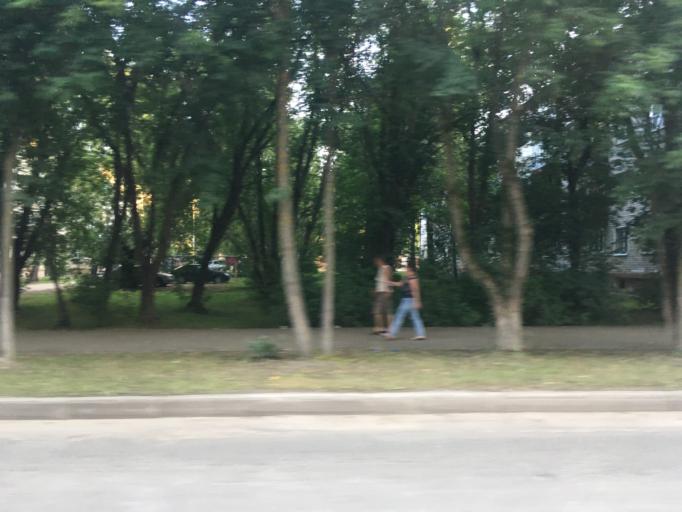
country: RU
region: Mariy-El
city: Yoshkar-Ola
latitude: 56.6478
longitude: 47.8814
